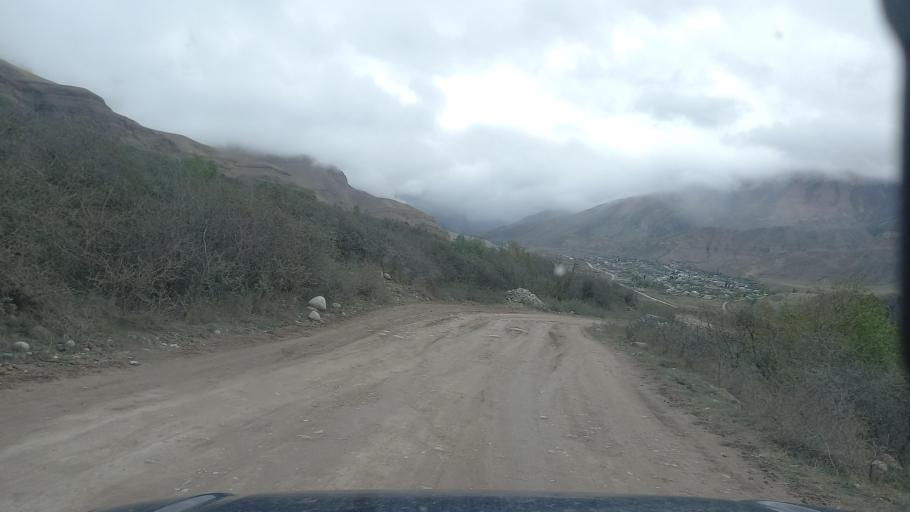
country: RU
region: Kabardino-Balkariya
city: Bylym
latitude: 43.4590
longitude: 43.0019
